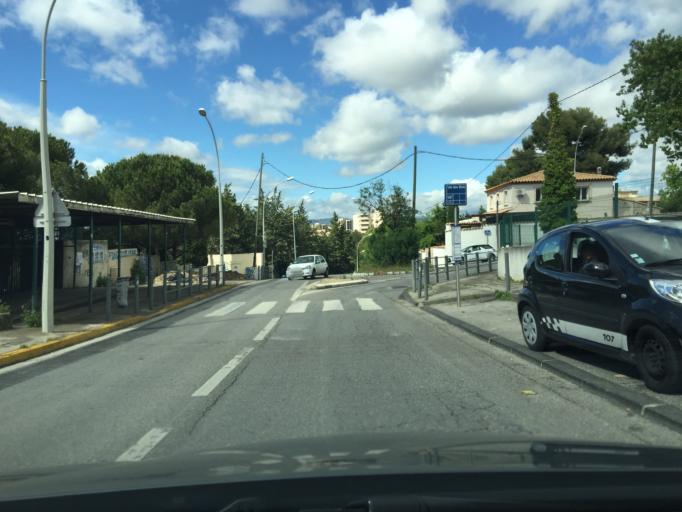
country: FR
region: Provence-Alpes-Cote d'Azur
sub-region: Departement des Bouches-du-Rhone
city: Marseille 10
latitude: 43.2642
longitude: 5.4227
